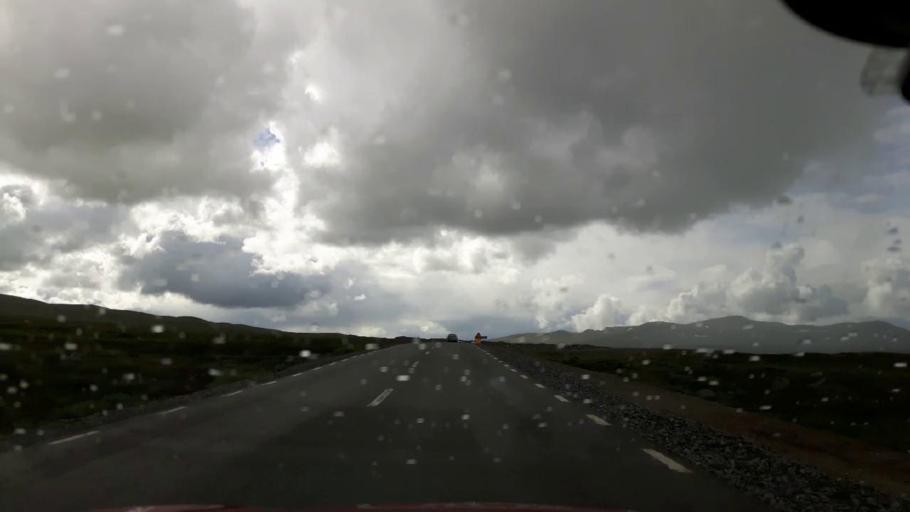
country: NO
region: Nordland
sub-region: Hattfjelldal
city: Hattfjelldal
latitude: 65.0987
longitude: 14.4674
